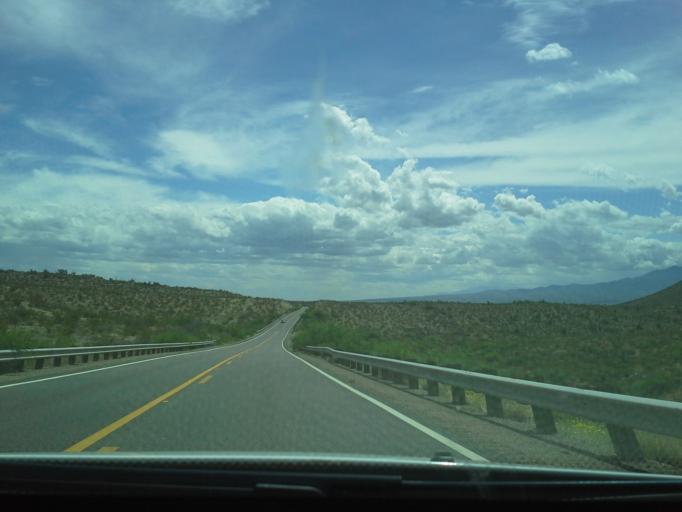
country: US
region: Arizona
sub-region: Gila County
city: Peridot
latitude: 33.2793
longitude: -110.3335
